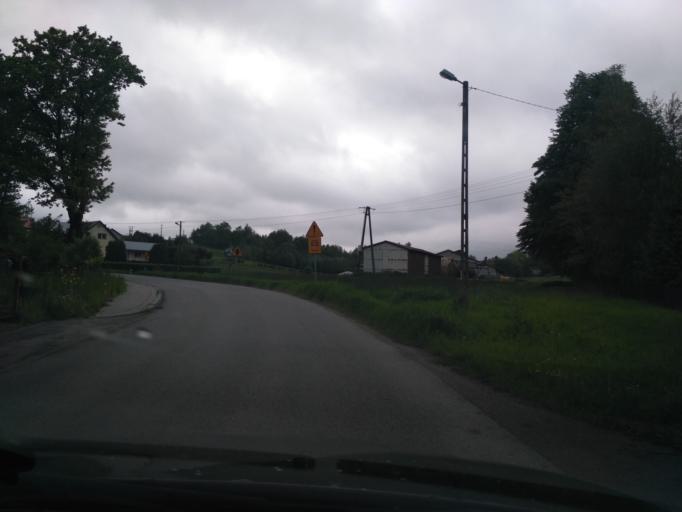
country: PL
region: Subcarpathian Voivodeship
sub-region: Powiat strzyzowski
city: Frysztak
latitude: 49.8053
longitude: 21.5815
